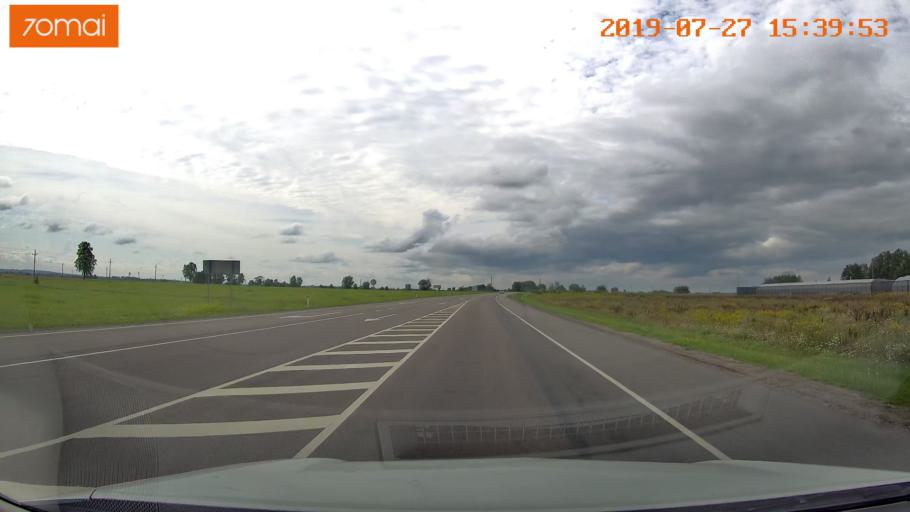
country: RU
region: Kaliningrad
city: Gusev
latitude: 54.6049
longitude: 22.2755
